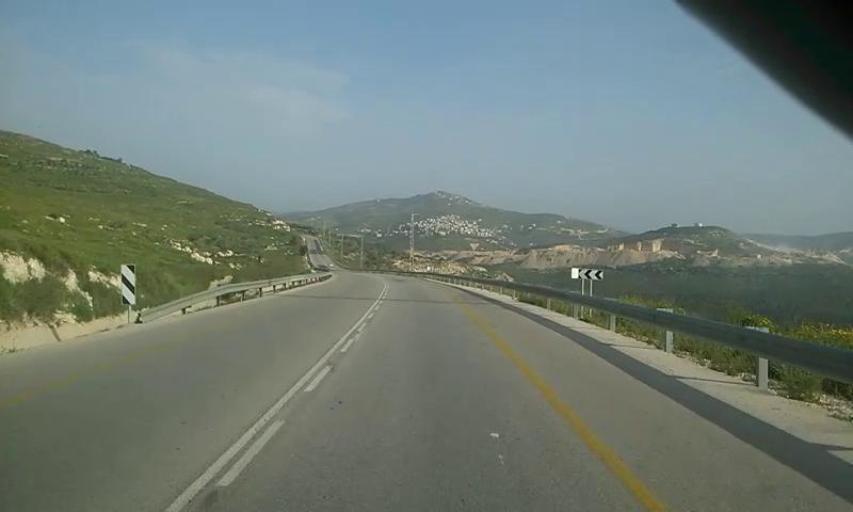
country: PS
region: West Bank
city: Sarrah
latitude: 32.1934
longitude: 35.1896
